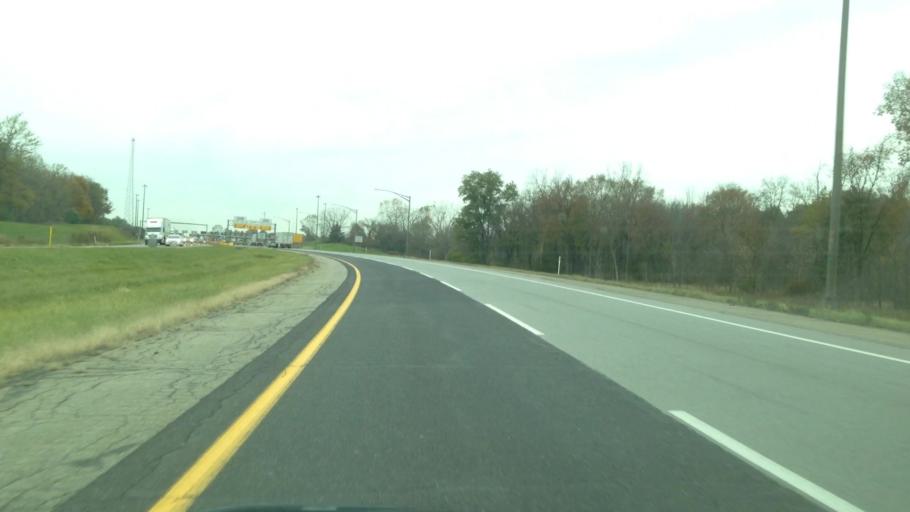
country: US
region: Indiana
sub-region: Steuben County
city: Fremont
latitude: 41.6629
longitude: -84.8473
